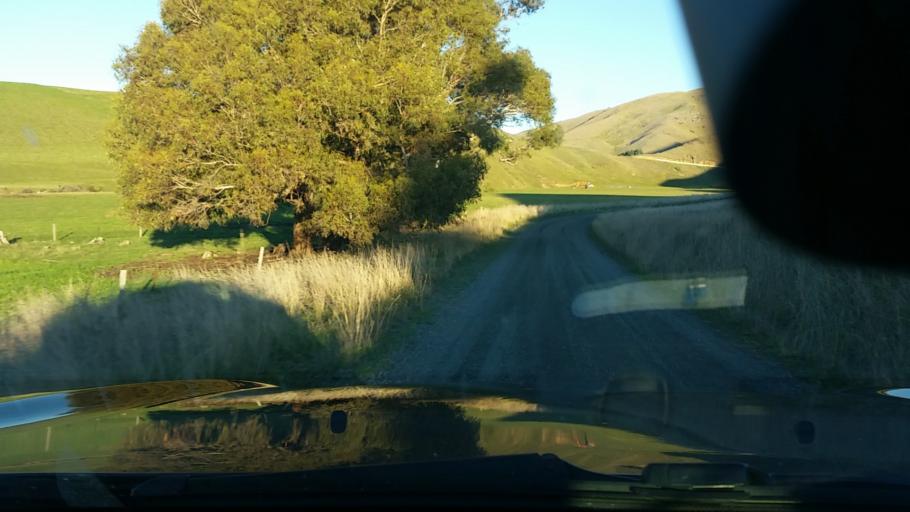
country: NZ
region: Marlborough
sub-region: Marlborough District
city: Blenheim
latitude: -41.7432
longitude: 174.0553
